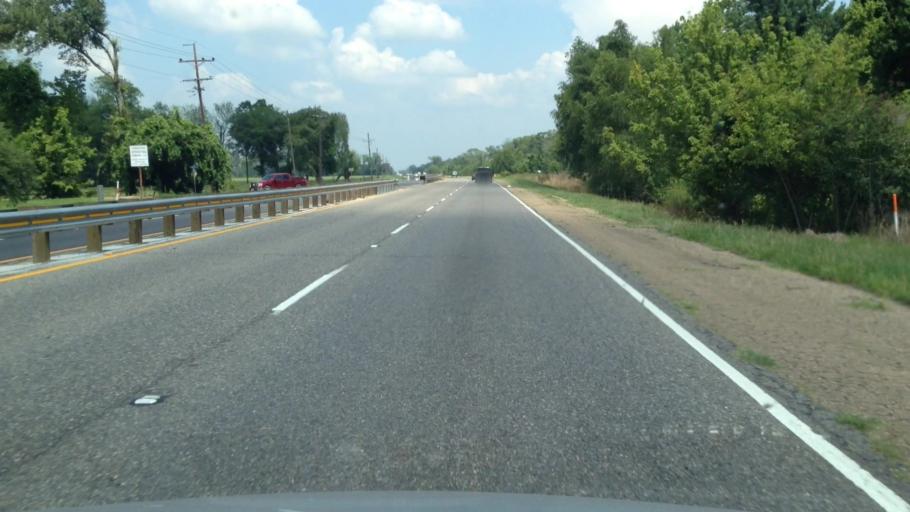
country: US
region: Louisiana
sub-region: Pointe Coupee Parish
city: Livonia
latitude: 30.5566
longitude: -91.6327
